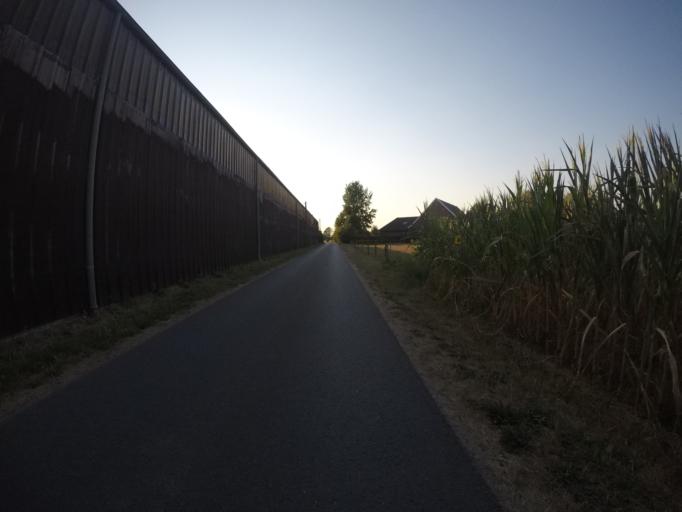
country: NL
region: Gelderland
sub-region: Gemeente Aalten
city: Aalten
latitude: 51.8631
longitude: 6.5402
